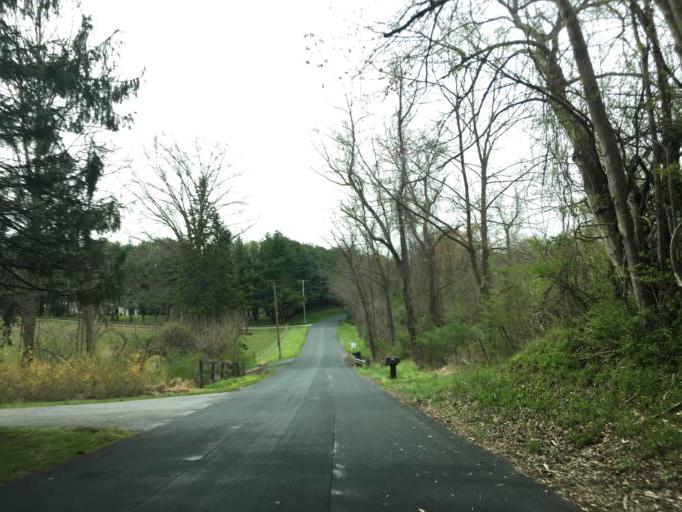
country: US
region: Maryland
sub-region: Baltimore County
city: Hunt Valley
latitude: 39.5693
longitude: -76.6276
